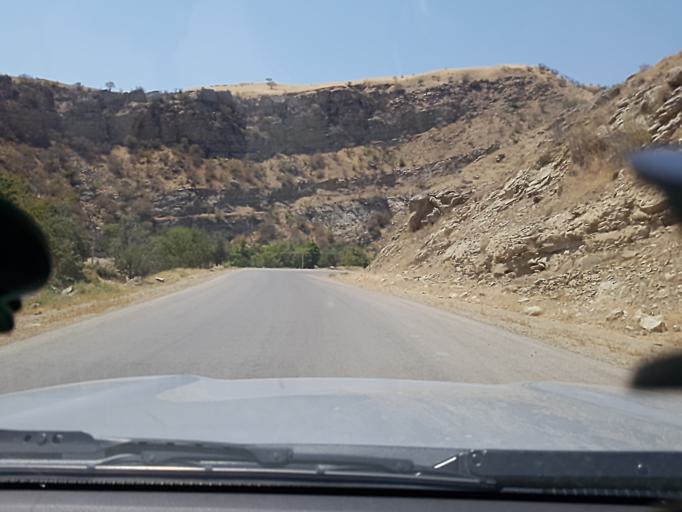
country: TM
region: Balkan
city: Magtymguly
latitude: 38.4211
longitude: 56.6103
